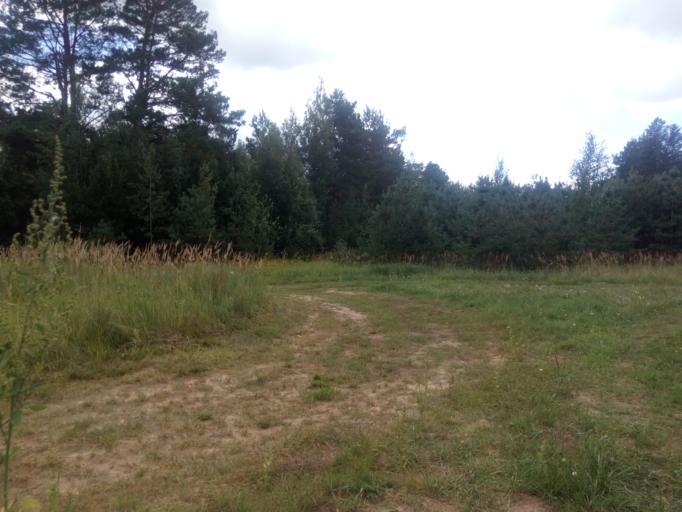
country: BY
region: Vitebsk
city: Dzisna
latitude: 55.6794
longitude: 28.2835
